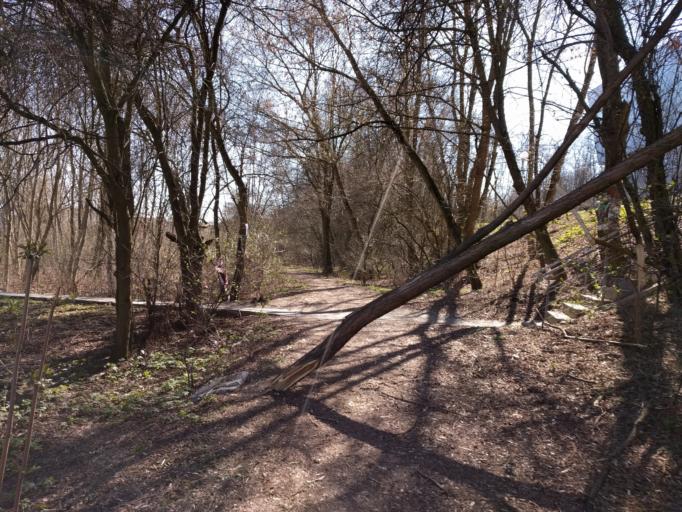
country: CZ
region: South Moravian
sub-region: Mesto Brno
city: Mokra Hora
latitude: 49.2314
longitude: 16.5740
